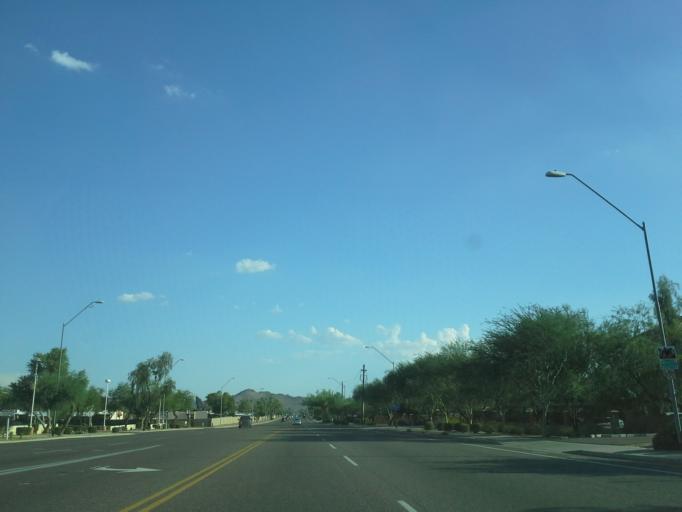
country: US
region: Arizona
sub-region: Maricopa County
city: Paradise Valley
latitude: 33.6545
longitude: -112.0309
